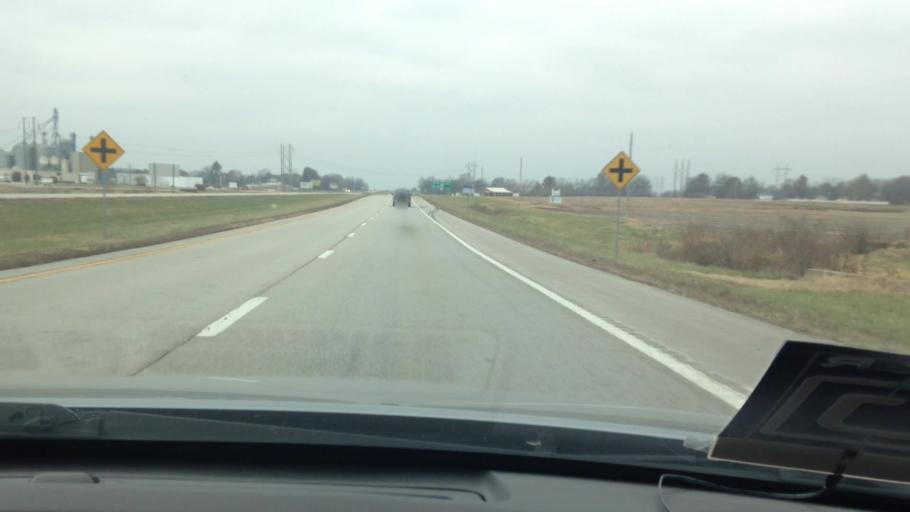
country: US
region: Missouri
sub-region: Cass County
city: Garden City
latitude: 38.5929
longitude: -94.2435
